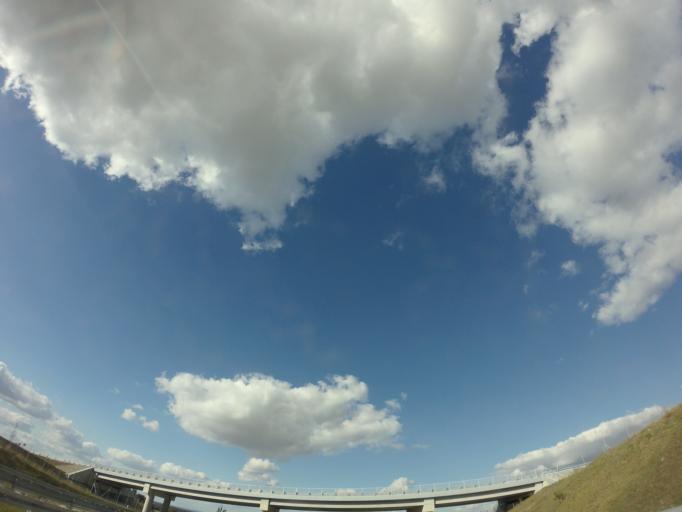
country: PL
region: Lower Silesian Voivodeship
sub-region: Powiat trzebnicki
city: Trzebnica
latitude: 51.3182
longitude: 17.0365
